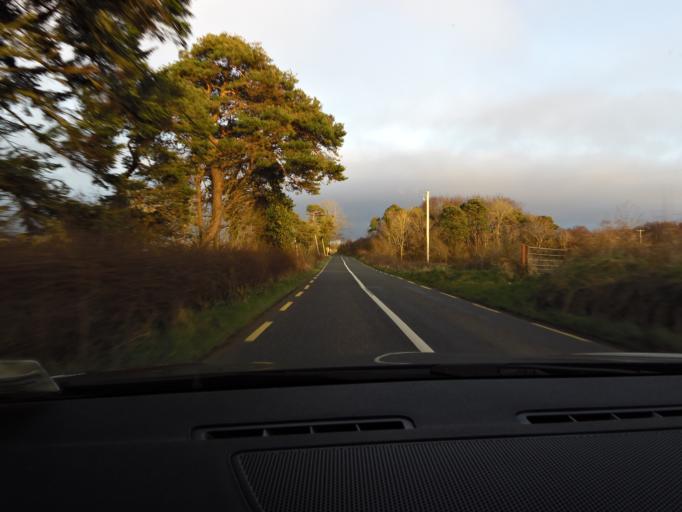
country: IE
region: Connaught
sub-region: Sligo
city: Ballymote
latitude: 54.0353
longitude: -8.6055
